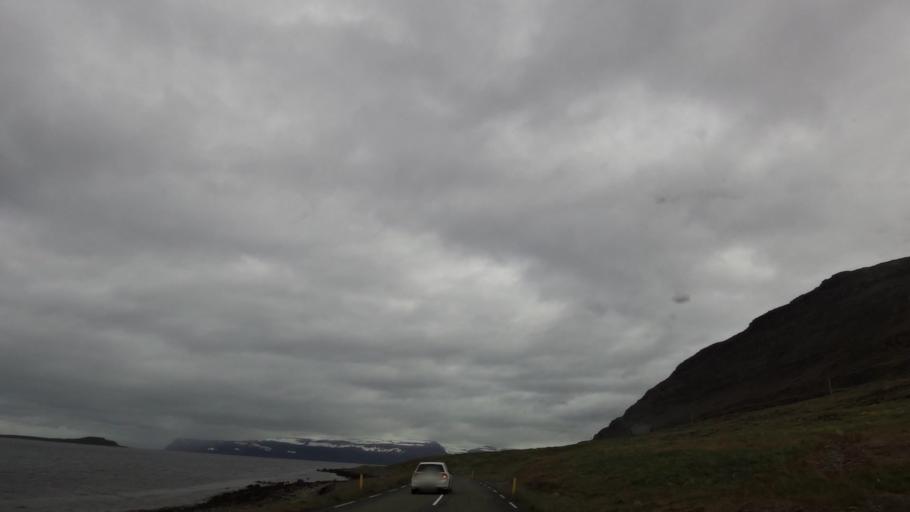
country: IS
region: Westfjords
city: Isafjoerdur
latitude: 66.0196
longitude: -22.7806
